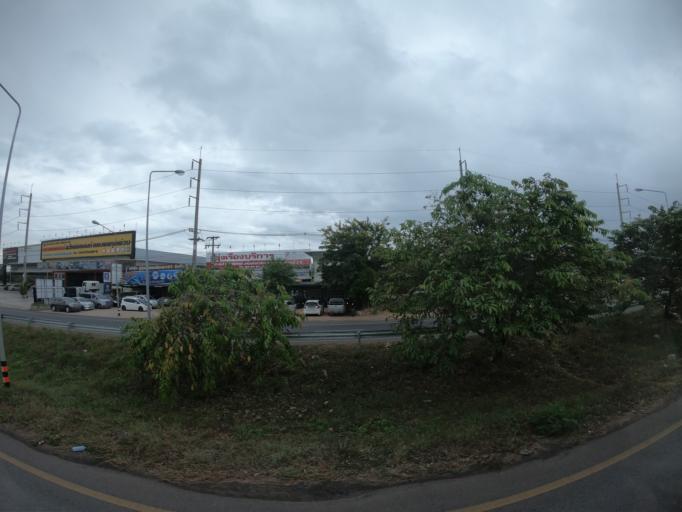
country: TH
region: Roi Et
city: Roi Et
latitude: 16.0498
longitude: 103.6208
